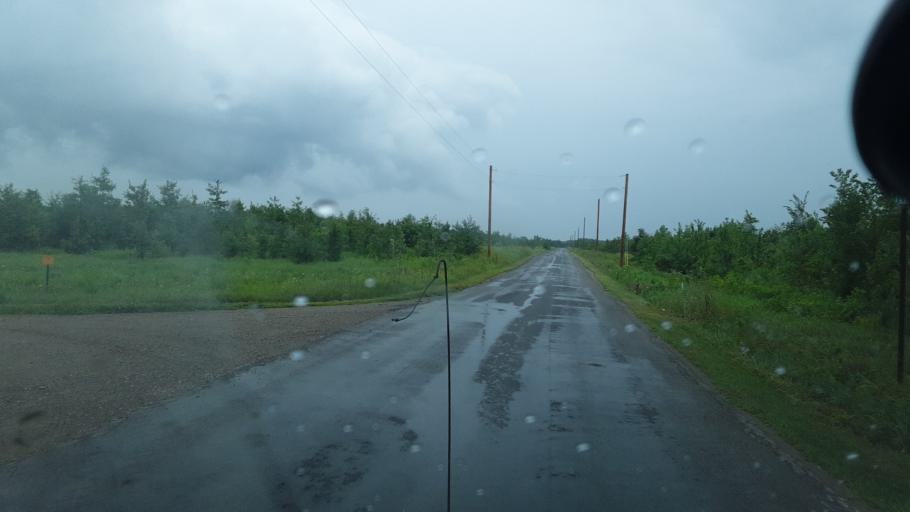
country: US
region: Indiana
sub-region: Steuben County
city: Hamilton
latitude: 41.5515
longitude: -84.8551
